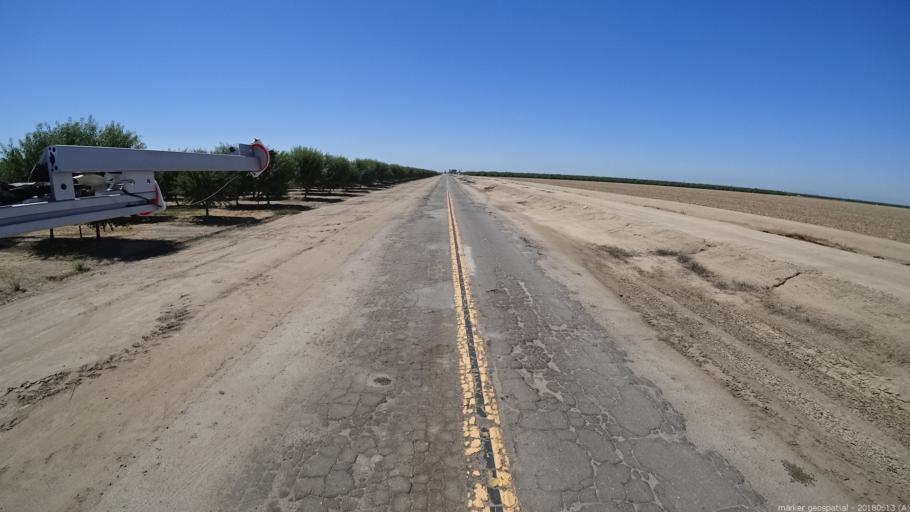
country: US
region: California
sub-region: Madera County
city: Chowchilla
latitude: 37.0755
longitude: -120.3650
